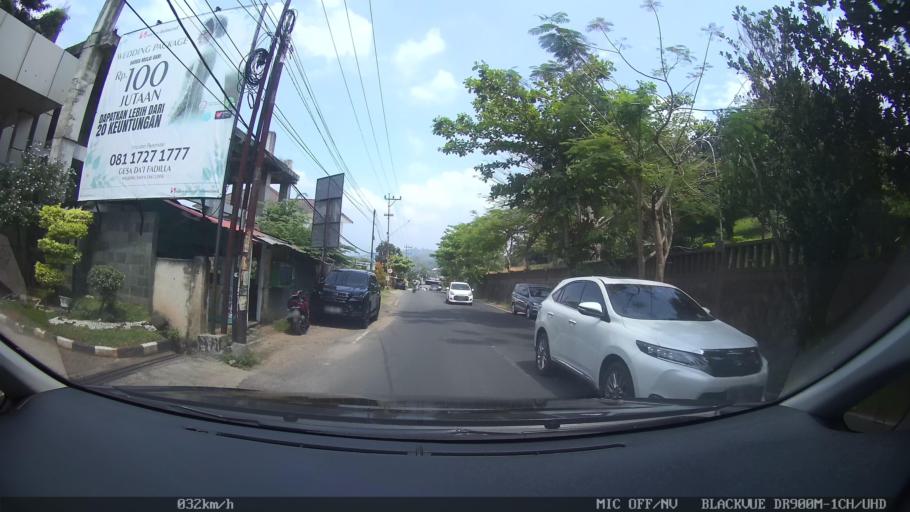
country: ID
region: Lampung
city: Bandarlampung
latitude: -5.4311
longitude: 105.2587
